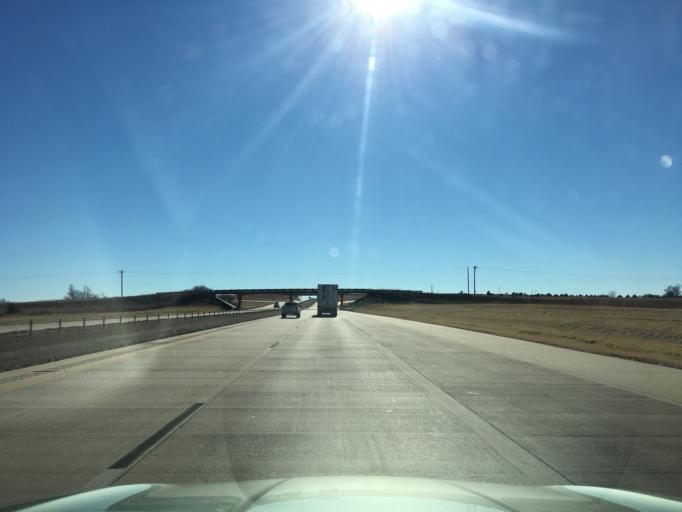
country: US
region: Oklahoma
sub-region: Noble County
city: Perry
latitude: 36.4078
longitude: -97.3272
